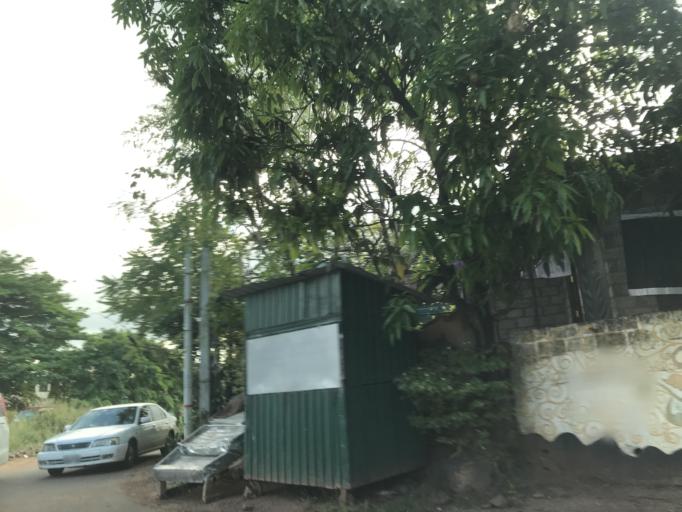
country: LK
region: Western
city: Gampaha
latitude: 7.0910
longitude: 79.9916
